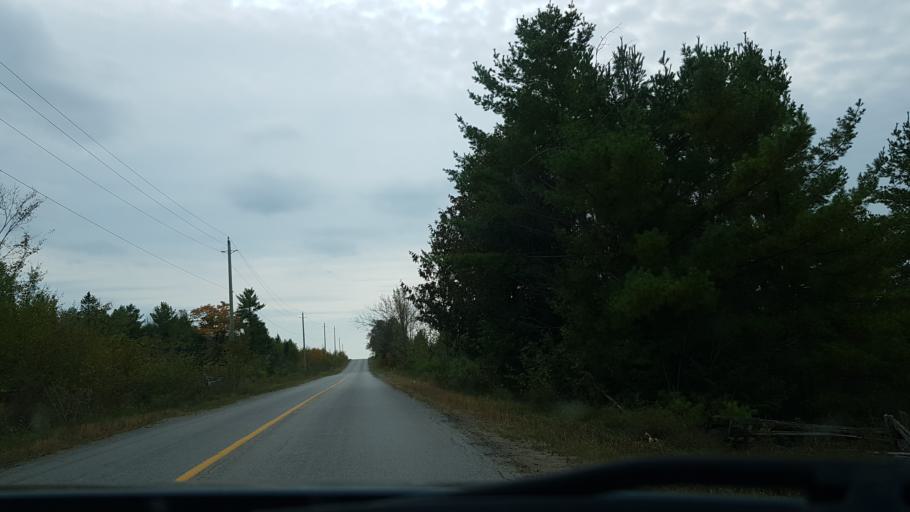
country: CA
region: Ontario
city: Orillia
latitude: 44.6567
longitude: -78.9679
